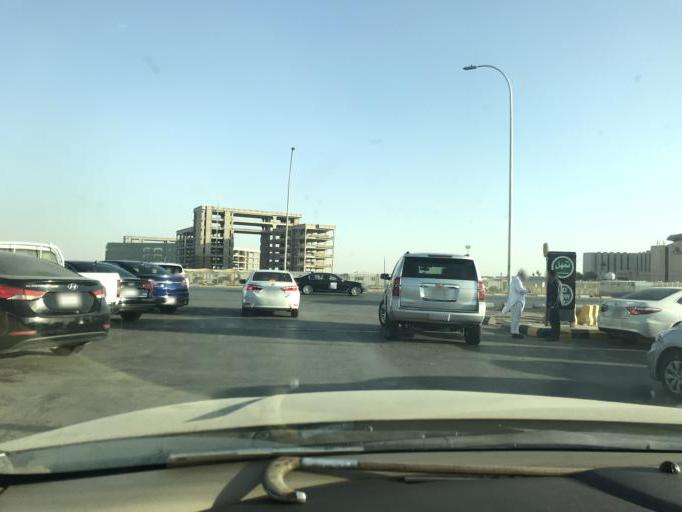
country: SA
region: Ar Riyad
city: Riyadh
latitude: 24.9282
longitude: 46.7135
